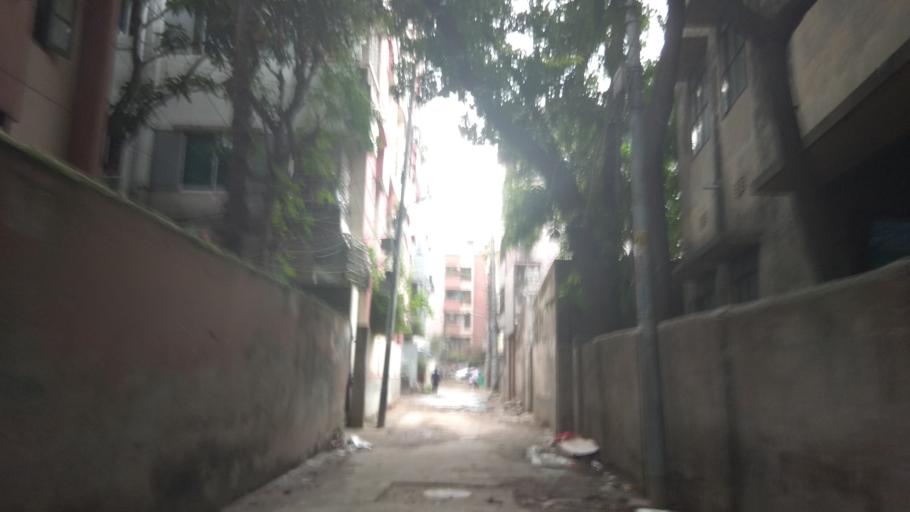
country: BD
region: Dhaka
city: Azimpur
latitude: 23.8019
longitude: 90.3754
